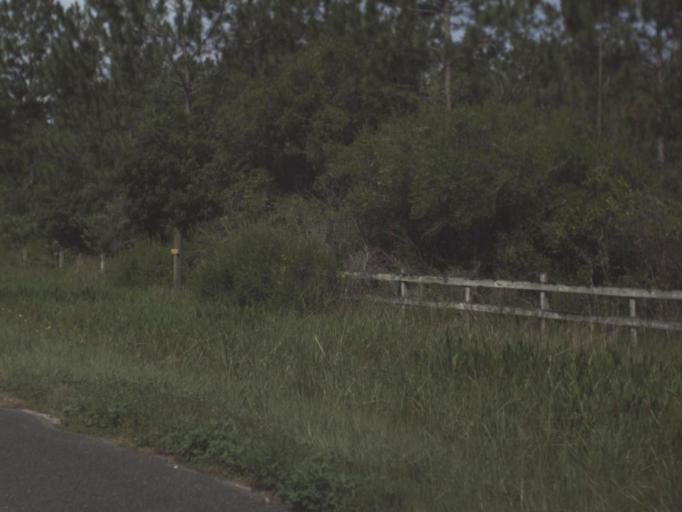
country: US
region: Florida
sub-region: Lafayette County
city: Mayo
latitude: 30.0288
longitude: -83.1860
